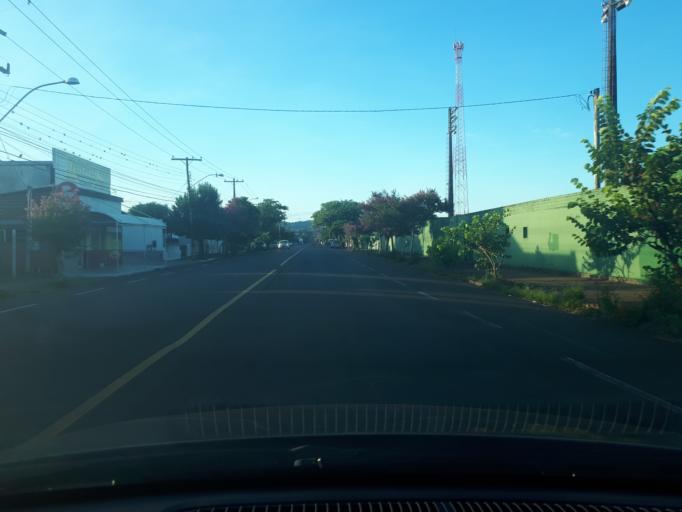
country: BR
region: Rio Grande do Sul
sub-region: Santa Cruz Do Sul
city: Santa Cruz do Sul
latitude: -29.7061
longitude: -52.4415
